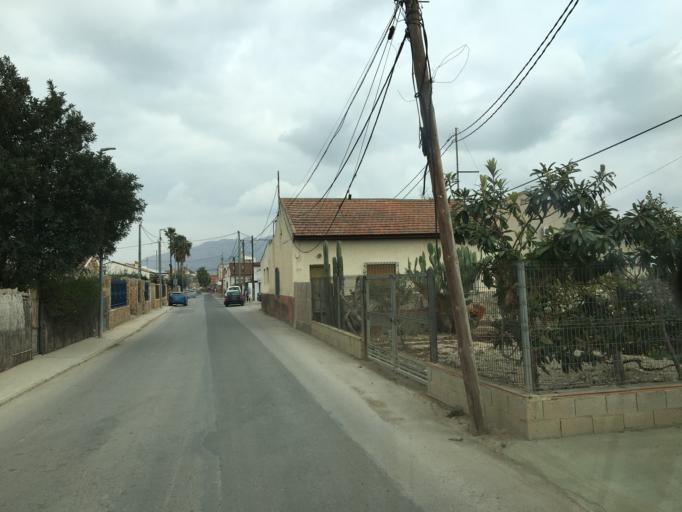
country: ES
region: Murcia
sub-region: Murcia
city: Beniel
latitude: 38.0435
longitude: -0.9920
